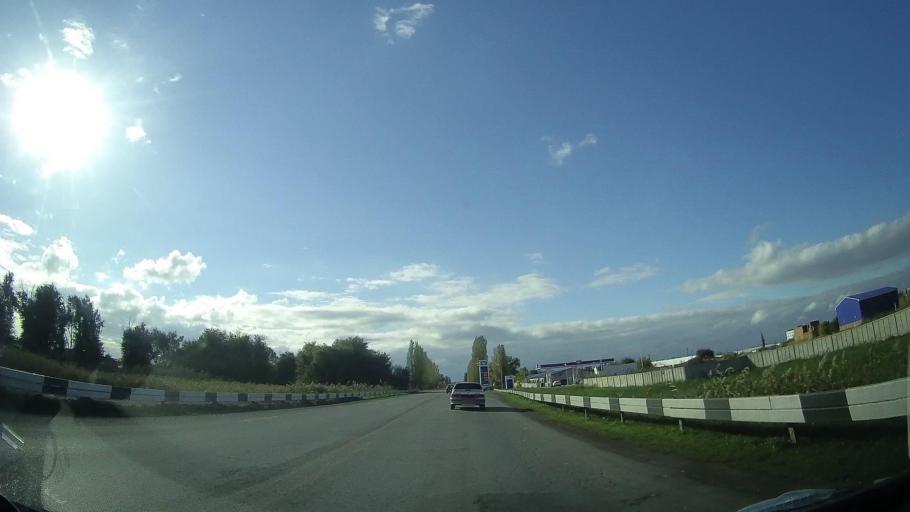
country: RU
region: Rostov
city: Tselina
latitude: 46.5318
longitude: 41.0076
